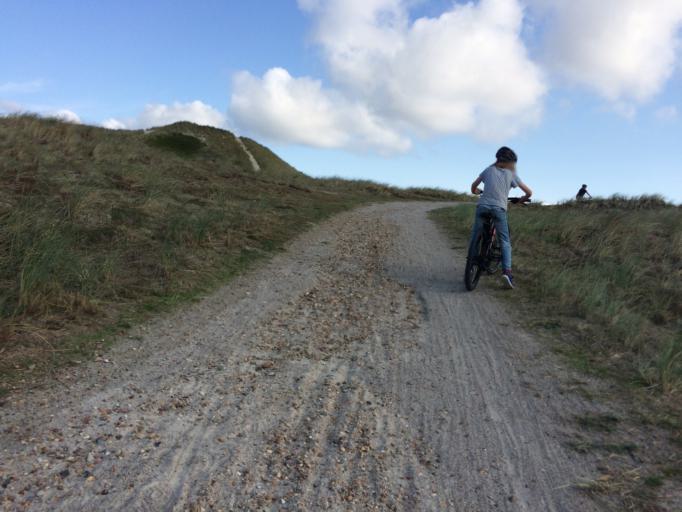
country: DK
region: Central Jutland
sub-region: Ringkobing-Skjern Kommune
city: Hvide Sande
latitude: 55.9107
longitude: 8.1567
